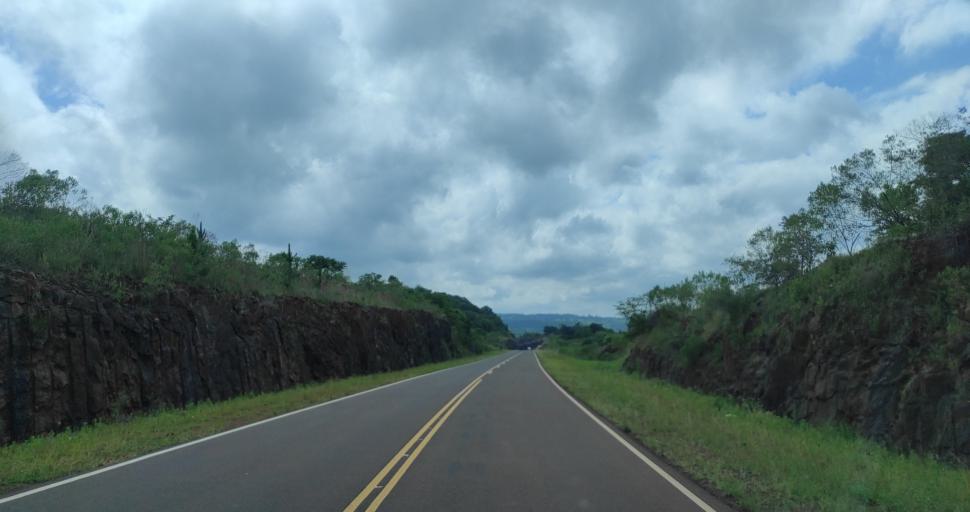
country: AR
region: Misiones
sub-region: Departamento de Veinticinco de Mayo
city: Veinticinco de Mayo
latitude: -27.3769
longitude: -54.8467
